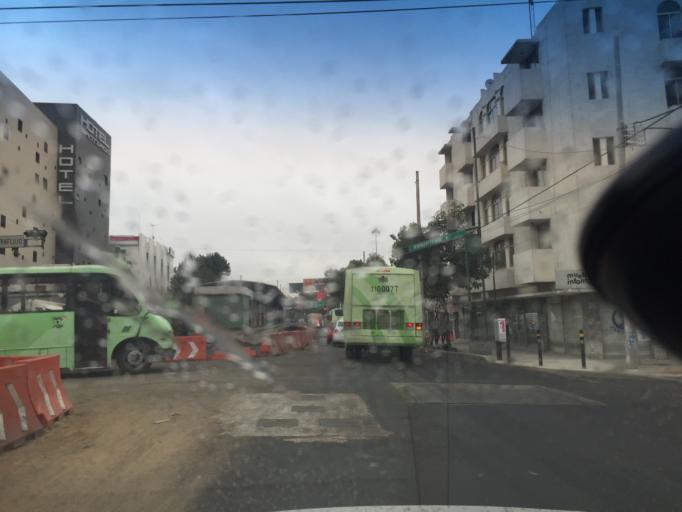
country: MX
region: Mexico
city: Colonia Lindavista
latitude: 19.4863
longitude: -99.1215
